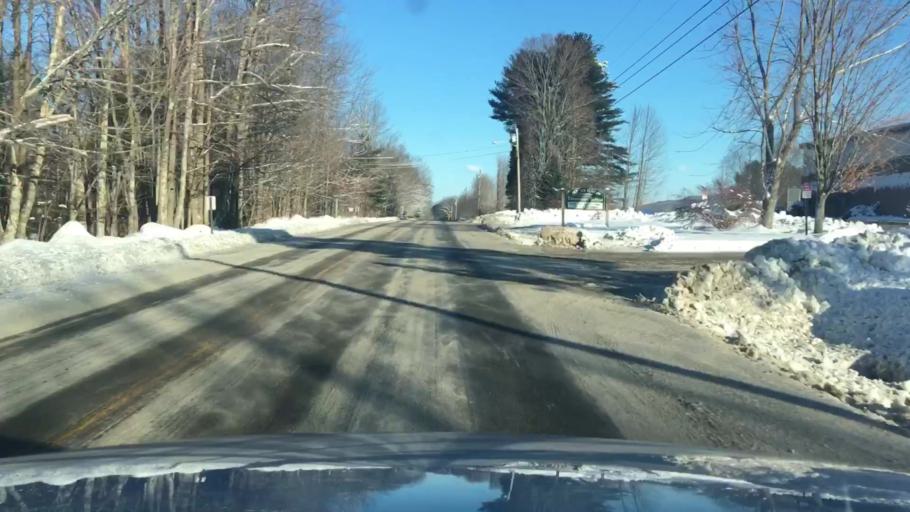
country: US
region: Maine
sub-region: Kennebec County
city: Mount Vernon
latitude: 44.4622
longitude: -69.9727
